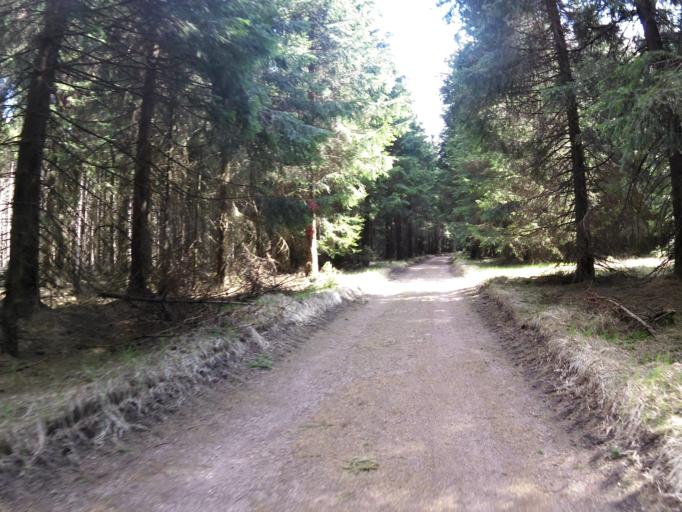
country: DE
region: Thuringia
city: Unterschonau
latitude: 50.7458
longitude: 10.5734
